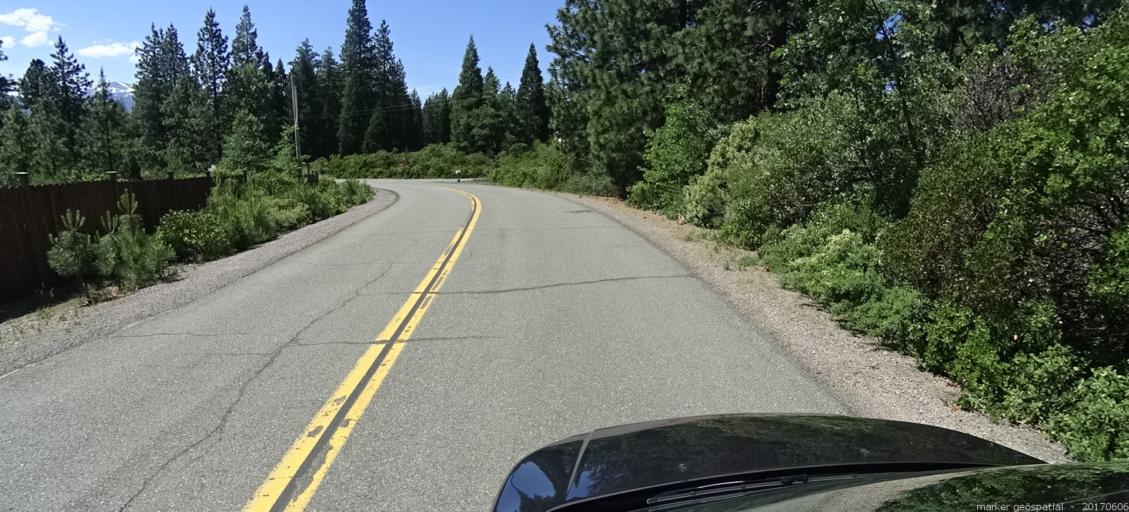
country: US
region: California
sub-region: Siskiyou County
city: Mount Shasta
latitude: 41.2832
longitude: -122.2942
